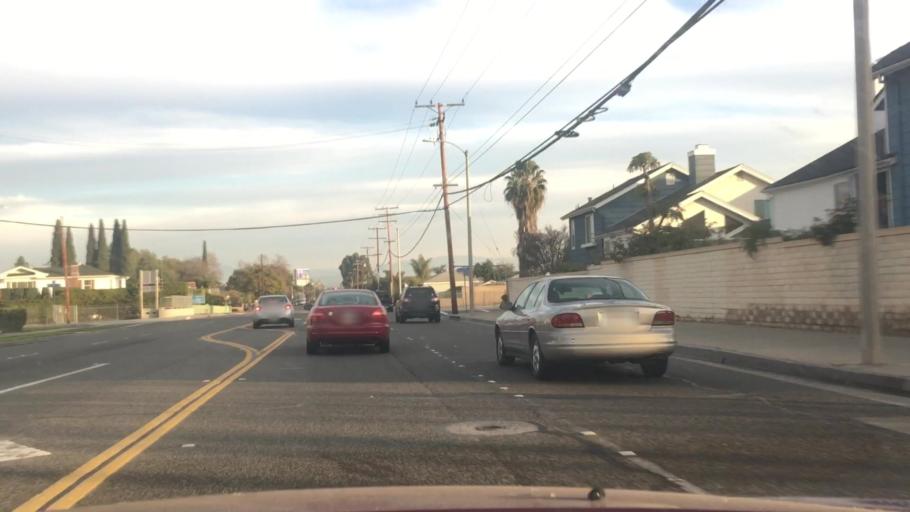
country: US
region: California
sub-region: Orange County
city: Buena Park
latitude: 33.8614
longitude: -118.0025
